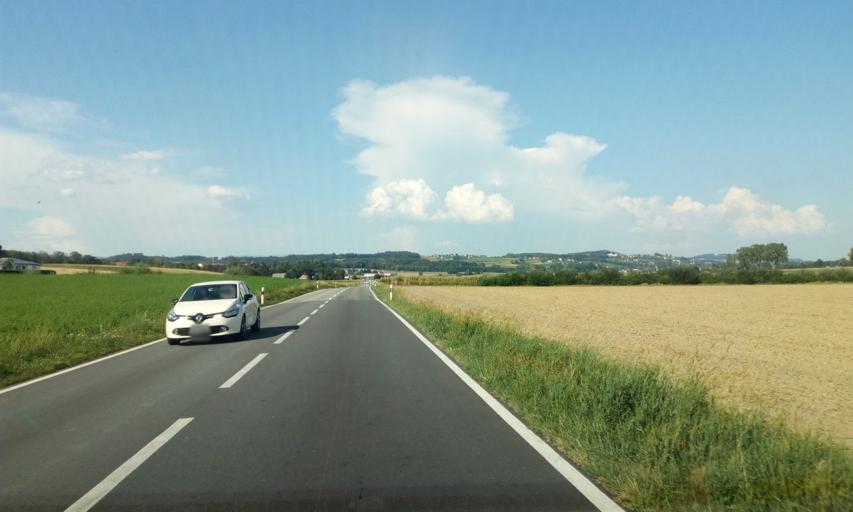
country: CH
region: Fribourg
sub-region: Broye District
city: Domdidier
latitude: 46.8923
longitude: 6.9881
